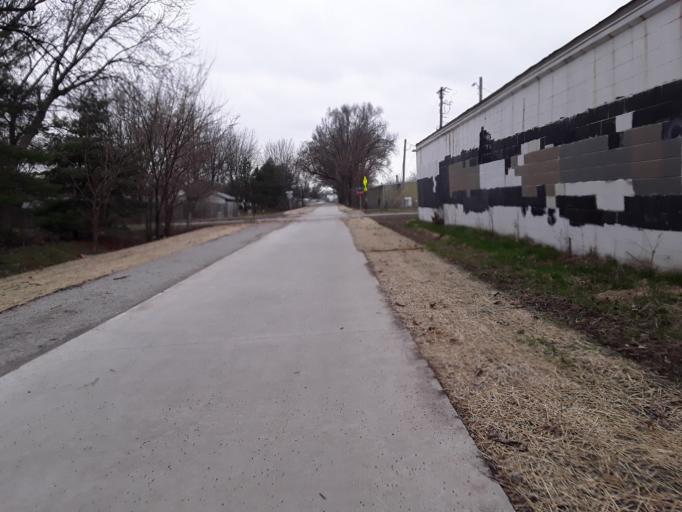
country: US
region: Nebraska
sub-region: Lancaster County
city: Lincoln
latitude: 40.8514
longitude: -96.6352
